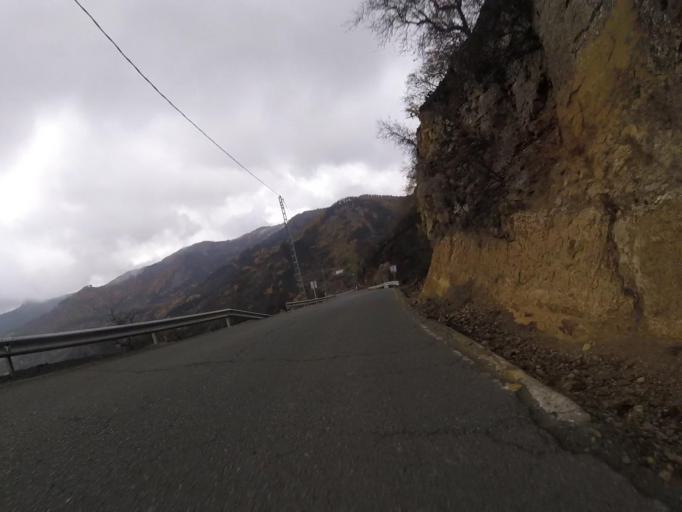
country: ES
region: Canary Islands
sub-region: Provincia de Las Palmas
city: Tejeda
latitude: 27.9879
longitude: -15.5758
